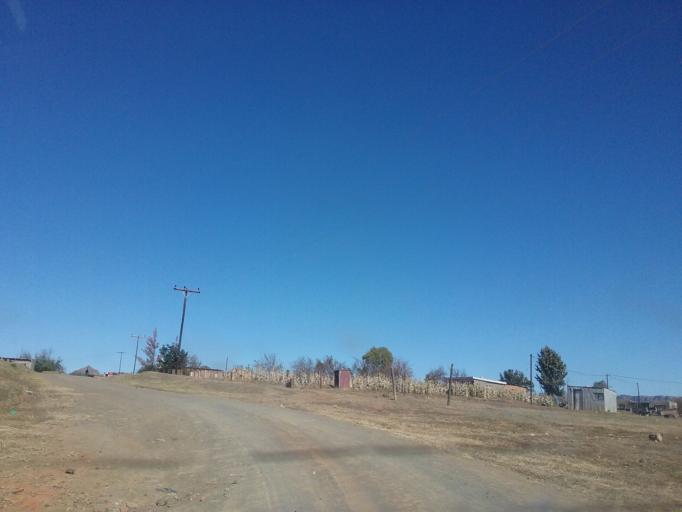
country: LS
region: Maseru
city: Maseru
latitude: -29.4505
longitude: 27.5780
